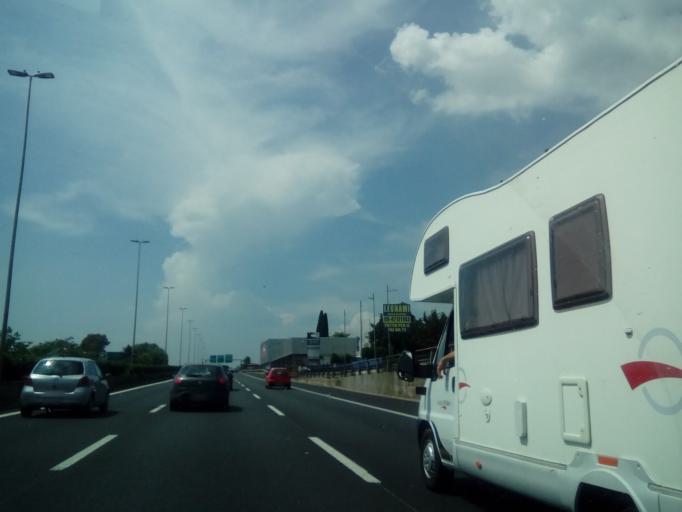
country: IT
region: Latium
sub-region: Citta metropolitana di Roma Capitale
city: Colle Verde
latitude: 41.9705
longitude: 12.5544
